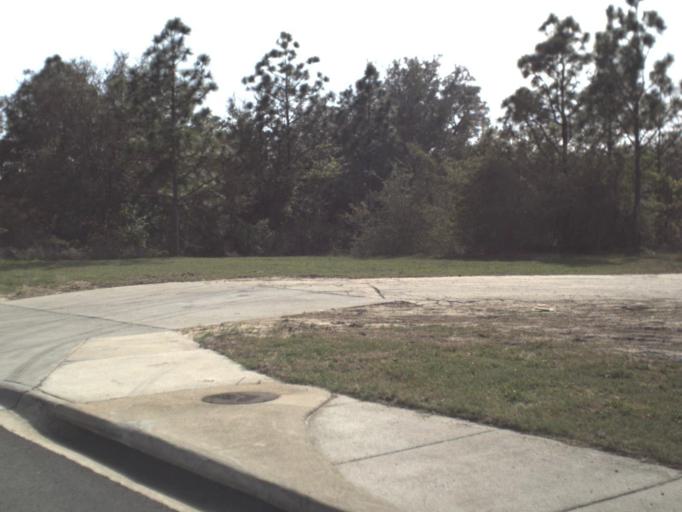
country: US
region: Florida
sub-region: Santa Rosa County
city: Navarre
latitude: 30.4083
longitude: -86.8707
